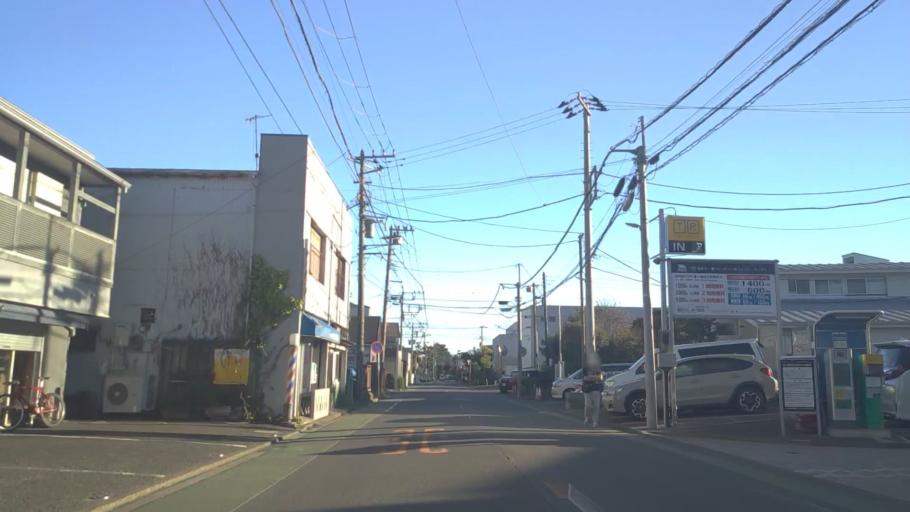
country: JP
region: Kanagawa
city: Chigasaki
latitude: 35.3248
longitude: 139.4149
